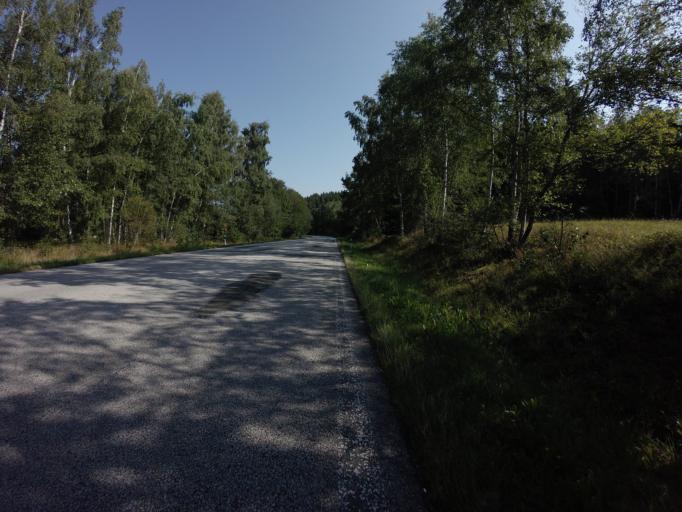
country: AT
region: Upper Austria
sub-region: Politischer Bezirk Urfahr-Umgebung
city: Bad Leonfelden
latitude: 48.5643
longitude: 14.3173
